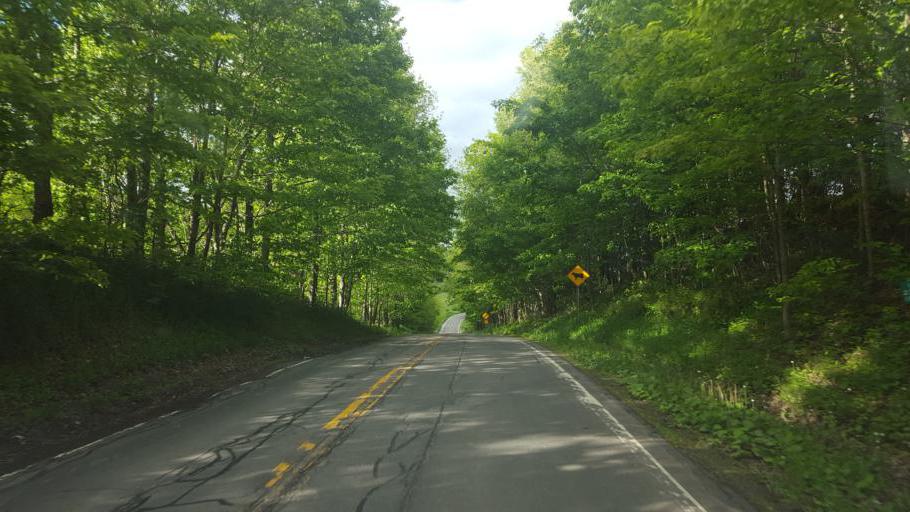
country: US
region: New York
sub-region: Otsego County
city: Richfield Springs
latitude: 42.8954
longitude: -74.9646
